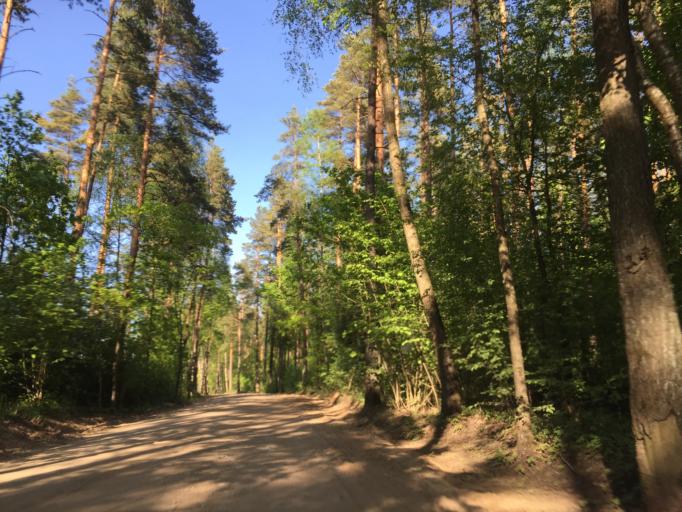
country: LV
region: Kekava
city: Kekava
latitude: 56.8179
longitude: 24.2308
